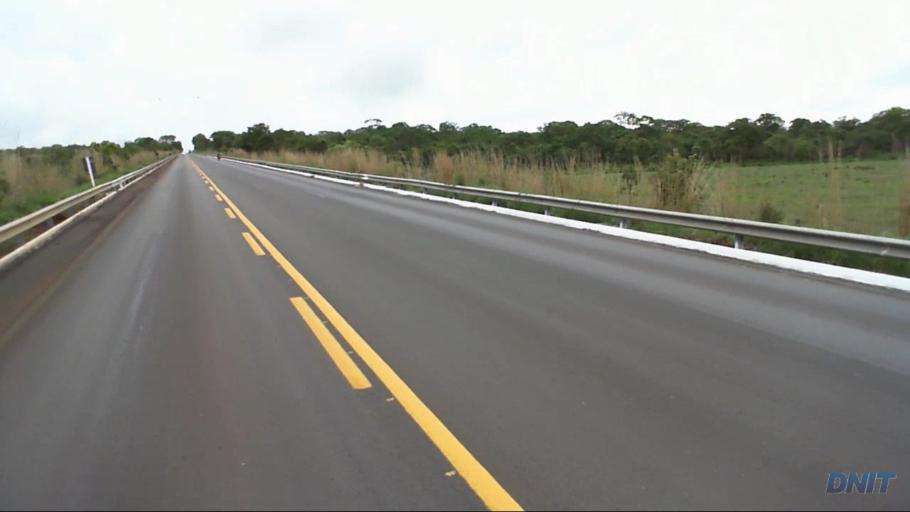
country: BR
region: Goias
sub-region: Padre Bernardo
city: Padre Bernardo
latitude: -15.1769
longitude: -48.4104
